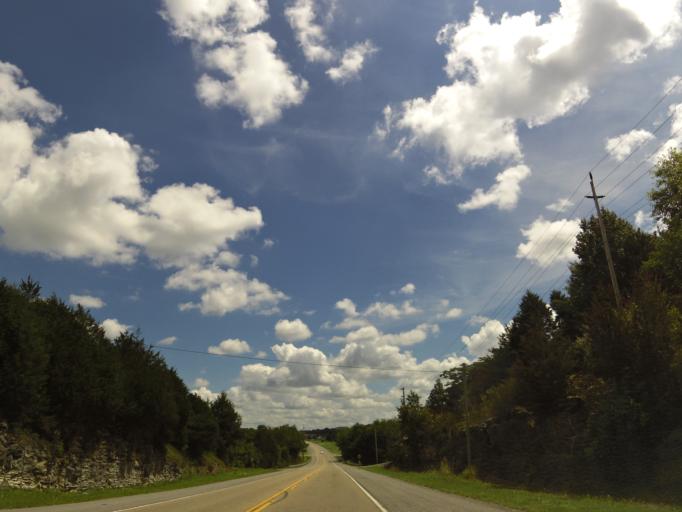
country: US
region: Kentucky
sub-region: Bell County
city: Middlesboro
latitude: 36.5295
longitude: -83.7213
